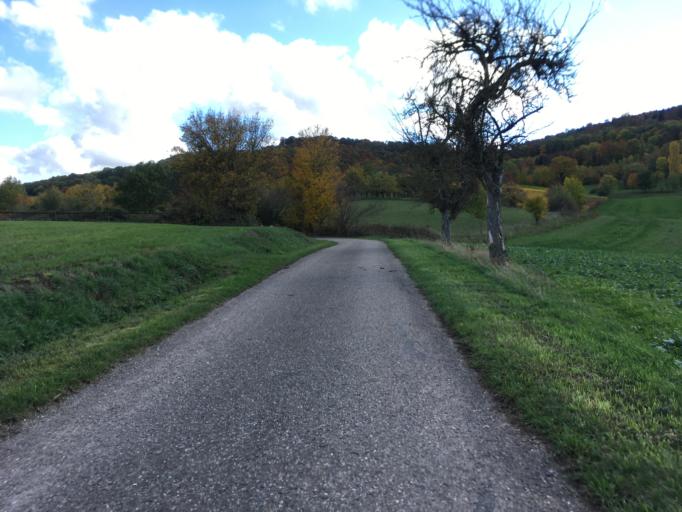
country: DE
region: Baden-Wuerttemberg
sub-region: Regierungsbezirk Stuttgart
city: Waldenburg
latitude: 49.1970
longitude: 9.6122
